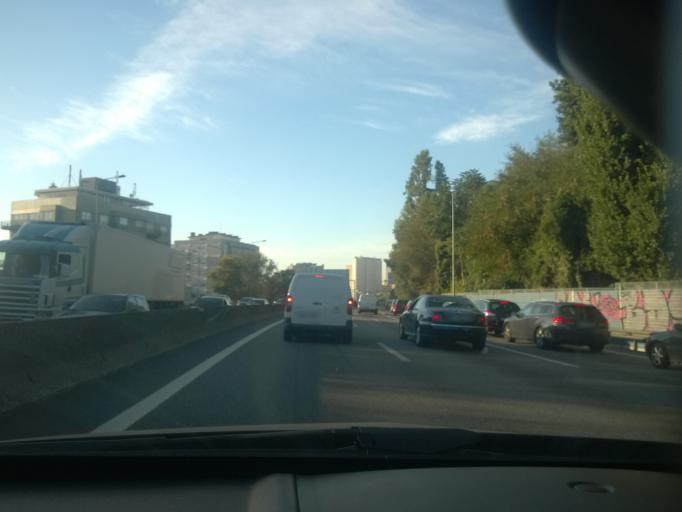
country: PT
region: Porto
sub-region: Vila Nova de Gaia
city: Canidelo
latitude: 41.1538
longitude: -8.6447
